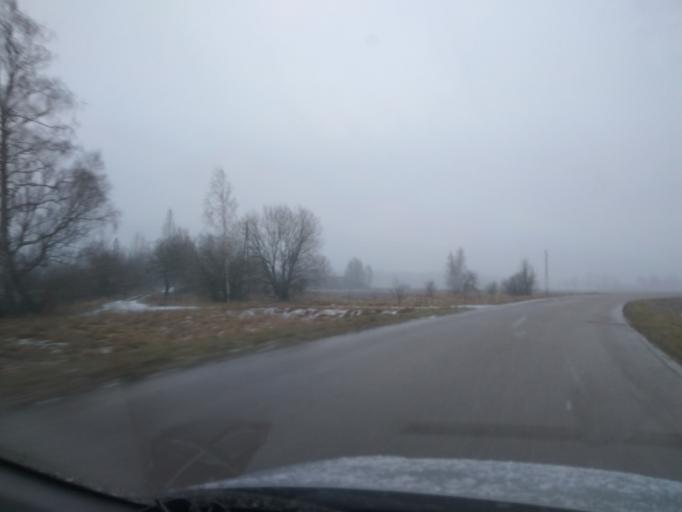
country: LV
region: Broceni
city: Broceni
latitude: 56.8495
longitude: 22.3871
